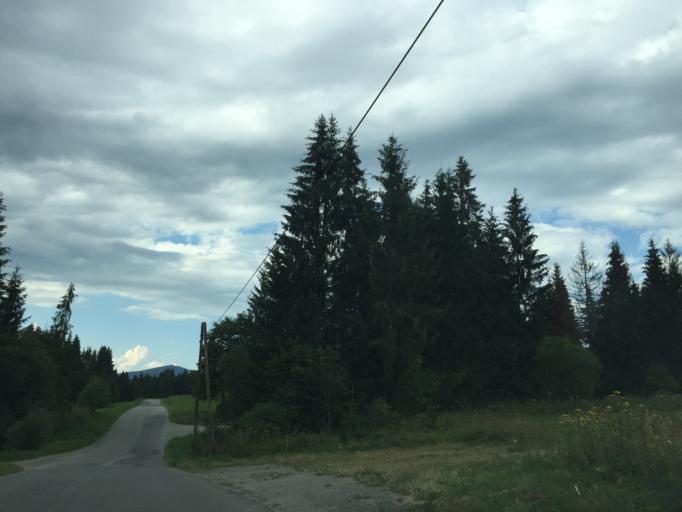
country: PL
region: Silesian Voivodeship
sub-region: Powiat zywiecki
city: Sopotnia Wielka
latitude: 49.4474
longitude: 19.3089
